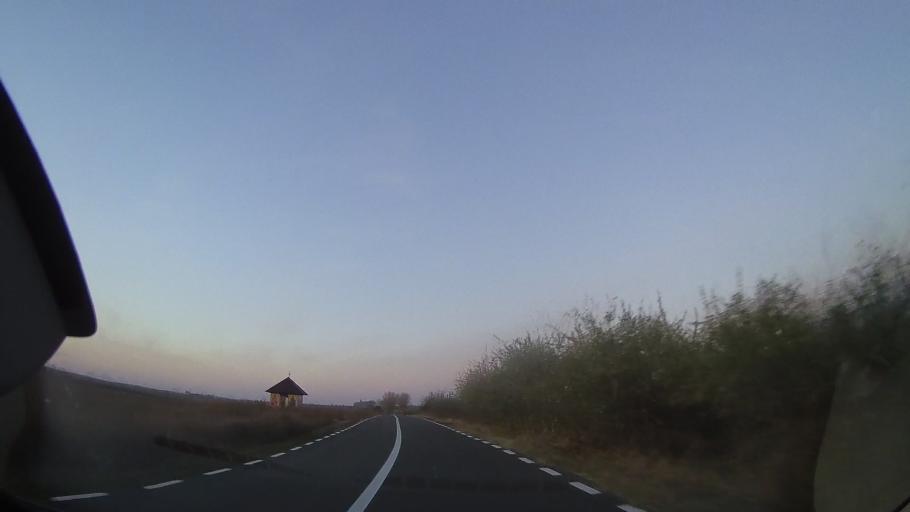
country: RO
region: Constanta
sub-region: Comuna Cobadin
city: Cobadin
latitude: 44.0350
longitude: 28.2599
